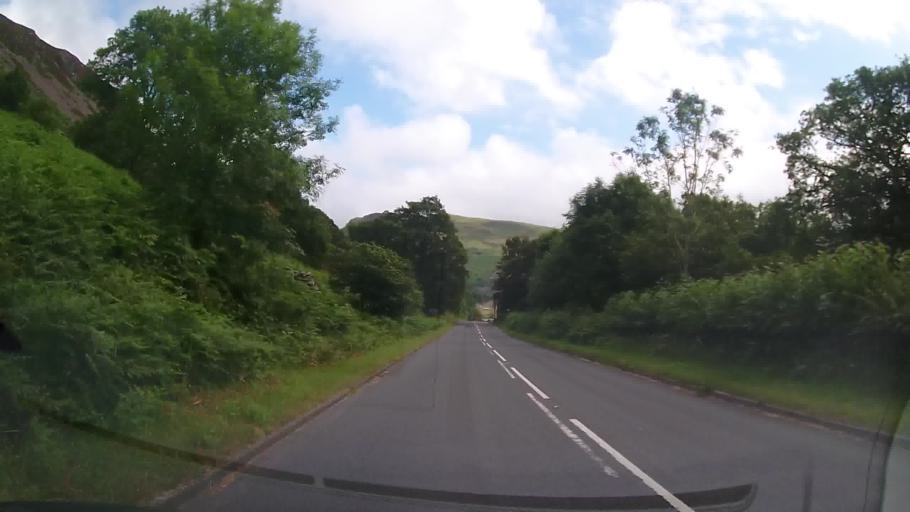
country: GB
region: Wales
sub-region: Sir Powys
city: Llangynog
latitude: 52.8309
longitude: -3.4141
